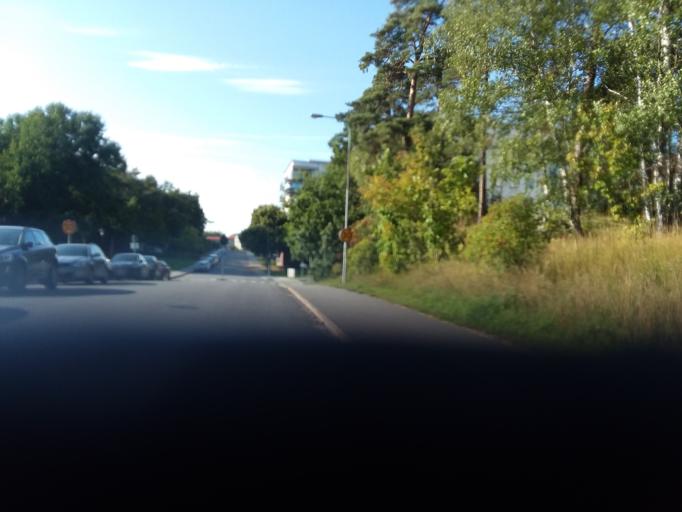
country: SE
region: Stockholm
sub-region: Stockholms Kommun
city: Bromma
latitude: 59.3538
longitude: 17.8773
